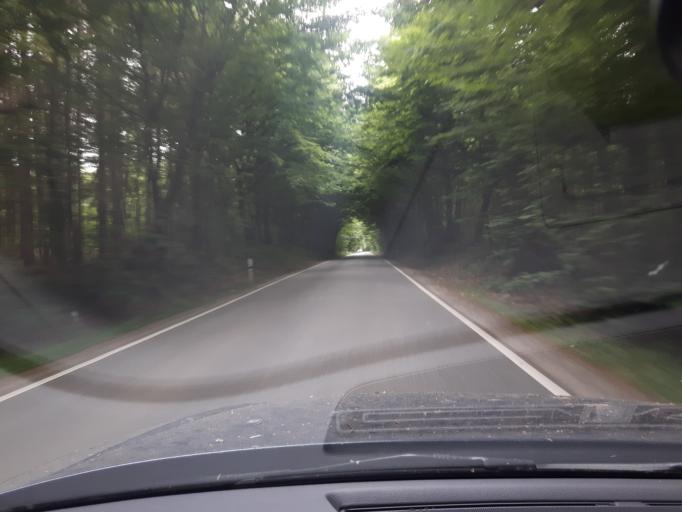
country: DE
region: Schleswig-Holstein
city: Ratekau
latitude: 53.9232
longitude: 10.7883
